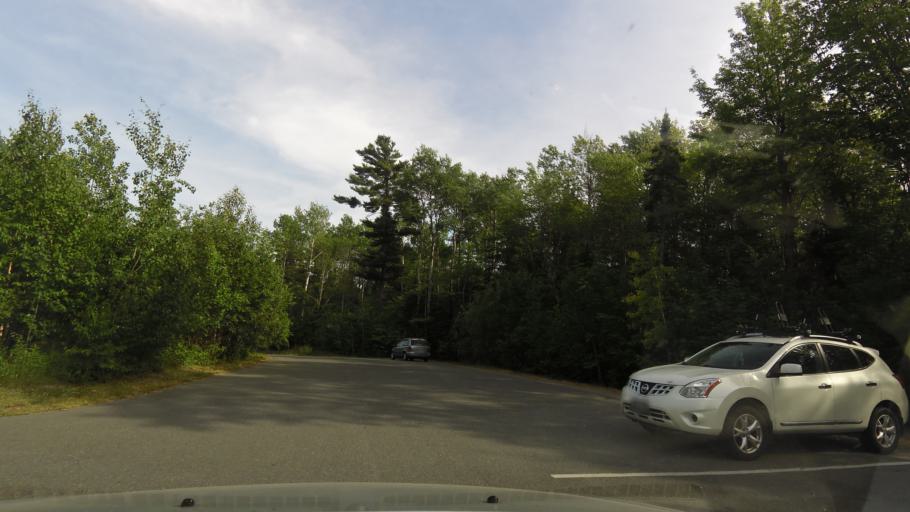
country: CA
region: Ontario
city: Greater Sudbury
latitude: 46.0158
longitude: -80.5846
